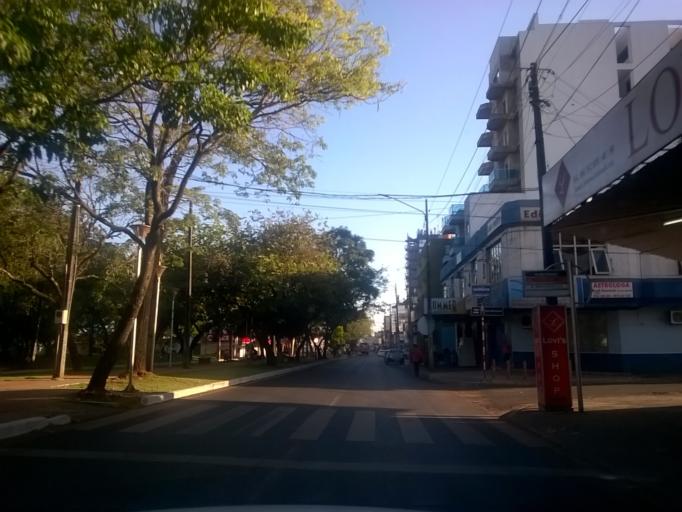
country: PY
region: Alto Parana
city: Presidente Franco
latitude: -25.5292
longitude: -54.6108
